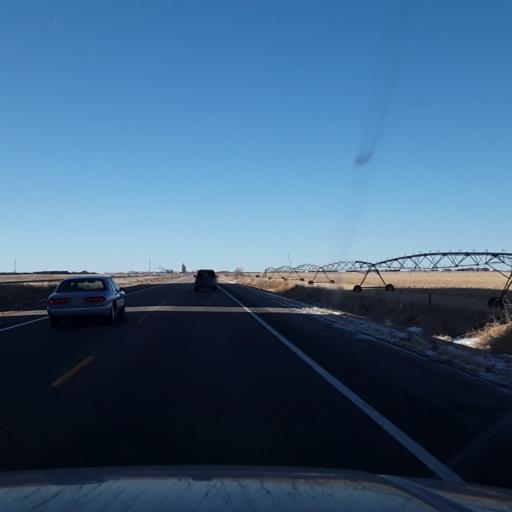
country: US
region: Nebraska
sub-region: Kearney County
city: Minden
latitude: 40.4918
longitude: -99.0297
